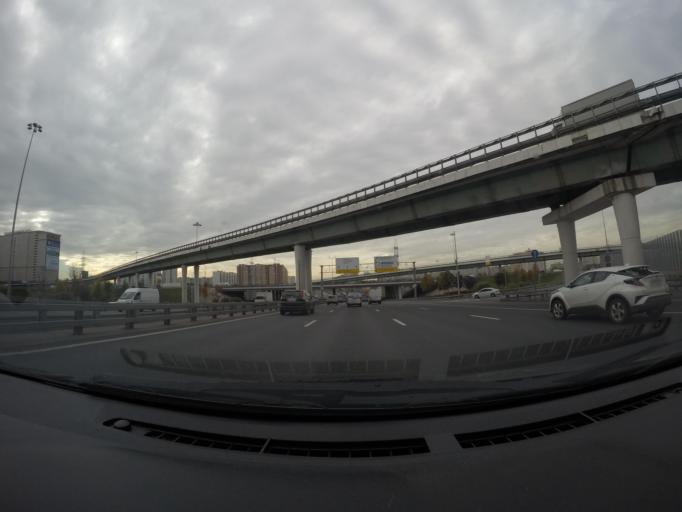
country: RU
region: Moscow
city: Yaroslavskiy
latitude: 55.8833
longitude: 37.7273
